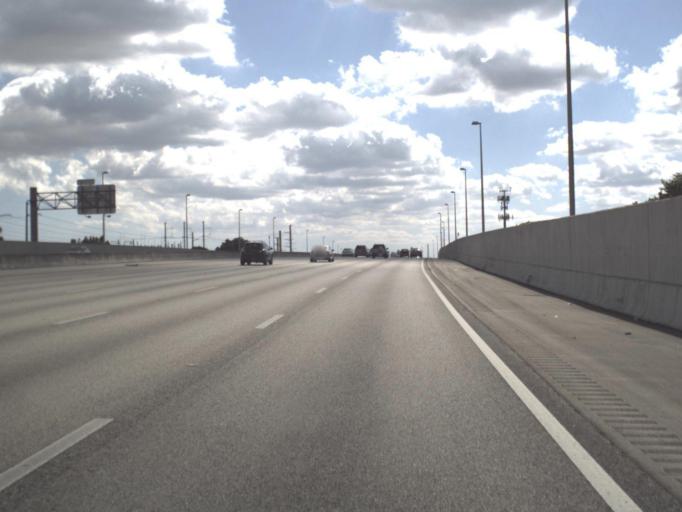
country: US
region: Florida
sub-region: Broward County
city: Lauderhill
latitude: 26.1236
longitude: -80.2179
